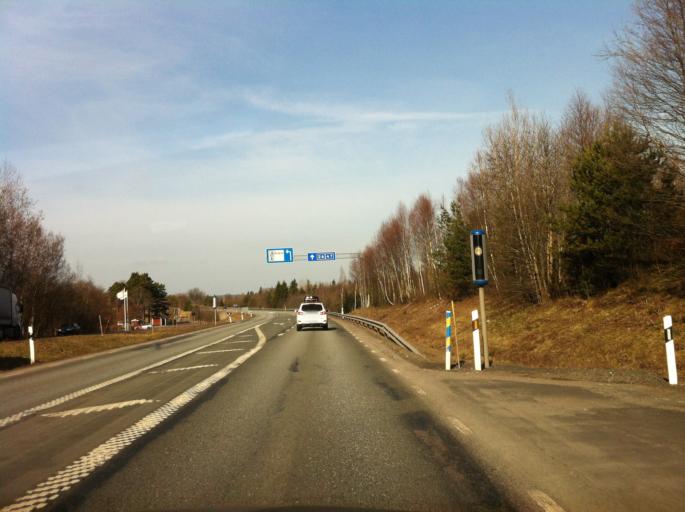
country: SE
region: Joenkoeping
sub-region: Habo Kommun
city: Habo
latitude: 57.8518
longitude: 14.0263
